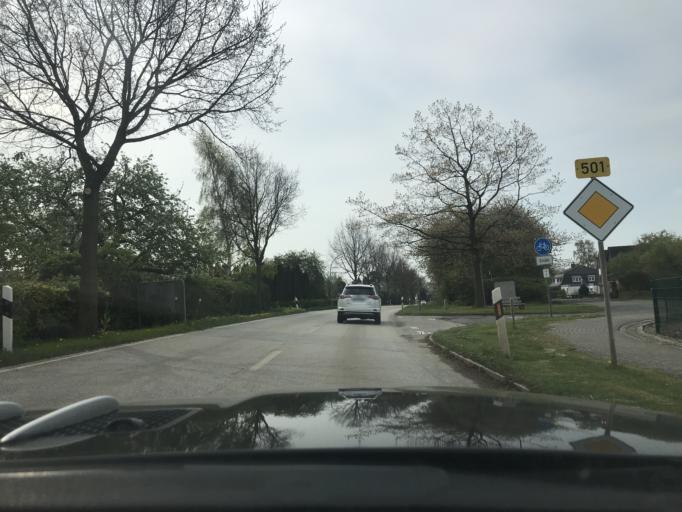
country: DE
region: Schleswig-Holstein
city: Heringsdorf
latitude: 54.2788
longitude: 11.0315
